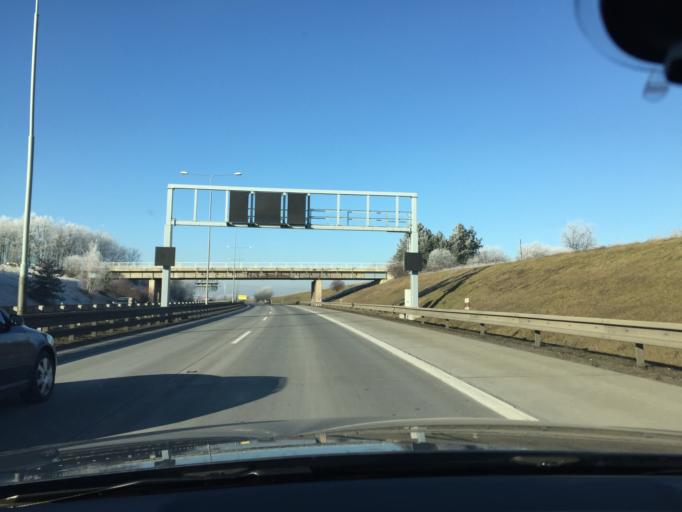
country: CZ
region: Central Bohemia
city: Cernosice
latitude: 50.0196
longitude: 14.3355
